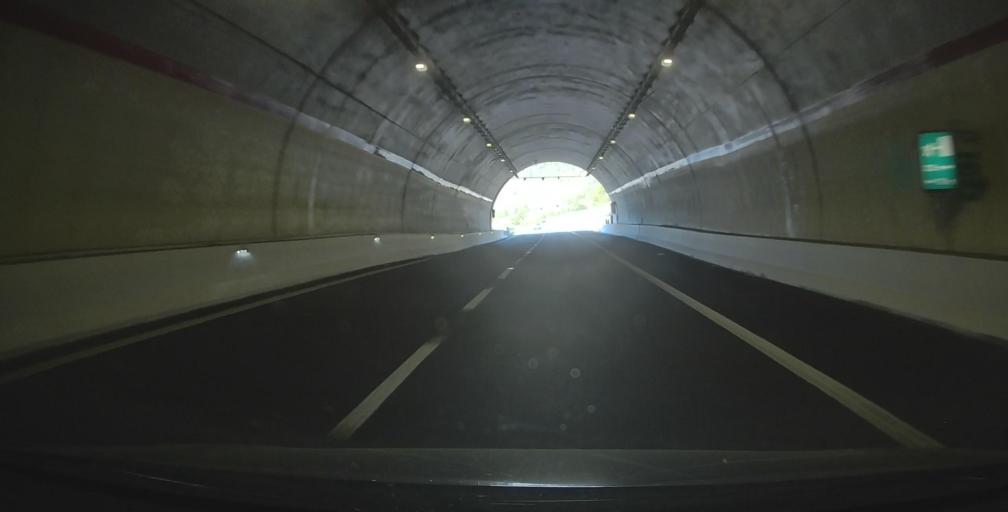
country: IT
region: Calabria
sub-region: Provincia di Cosenza
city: Mormanno
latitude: 39.8889
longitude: 16.0328
